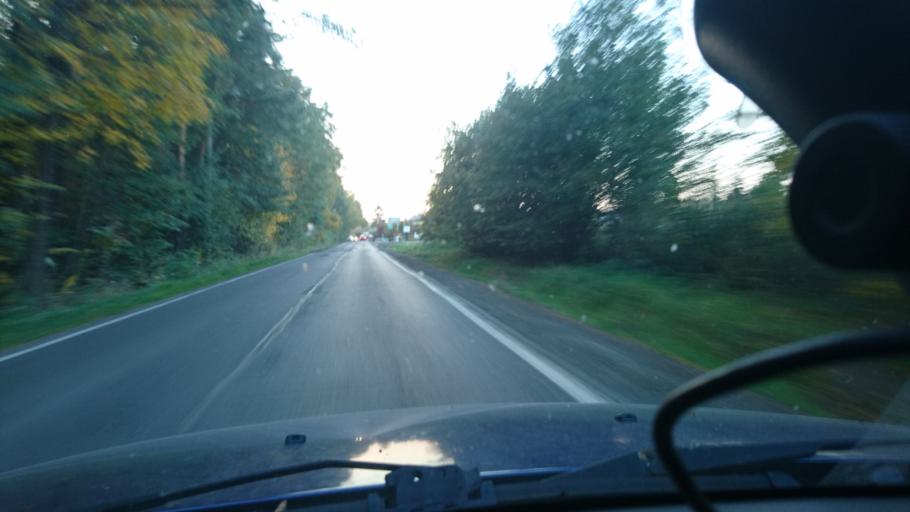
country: PL
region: Silesian Voivodeship
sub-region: Powiat bielski
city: Kozy
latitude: 49.8505
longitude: 19.1121
